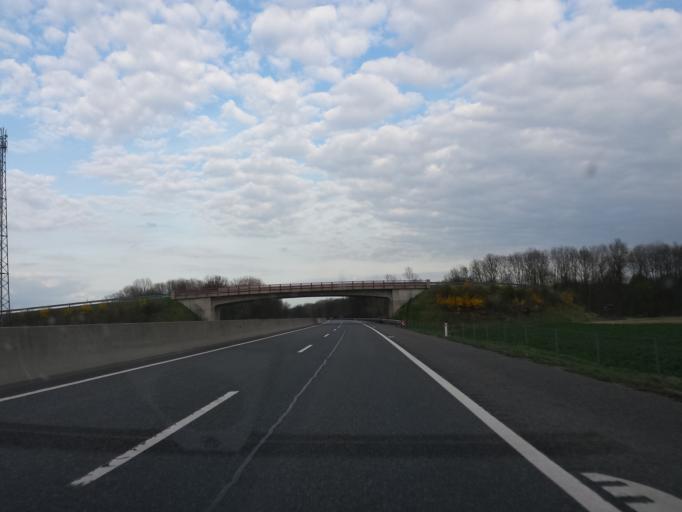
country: AT
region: Lower Austria
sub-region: Politischer Bezirk Korneuburg
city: Stetteldorf am Wagram
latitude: 48.3577
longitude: 16.0040
